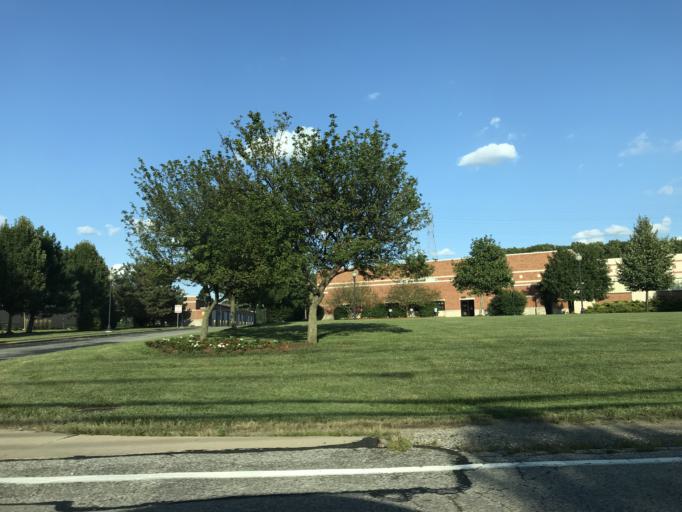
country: US
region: Ohio
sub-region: Cuyahoga County
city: Middleburg Heights
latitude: 41.3663
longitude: -81.8251
